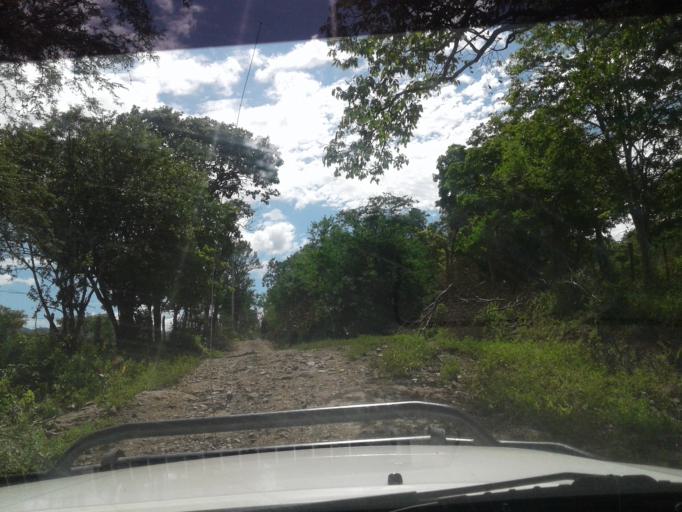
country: NI
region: Leon
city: Santa Rosa del Penon
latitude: 12.8755
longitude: -86.2438
